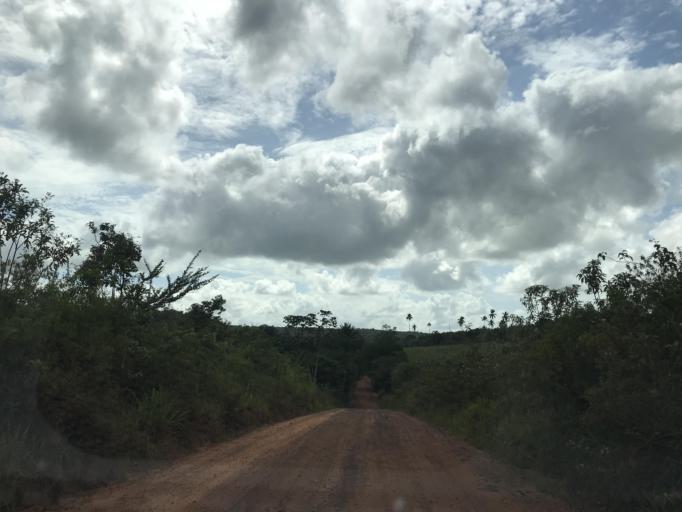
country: BR
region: Bahia
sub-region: Entre Rios
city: Entre Rios
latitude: -12.1743
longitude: -38.1320
